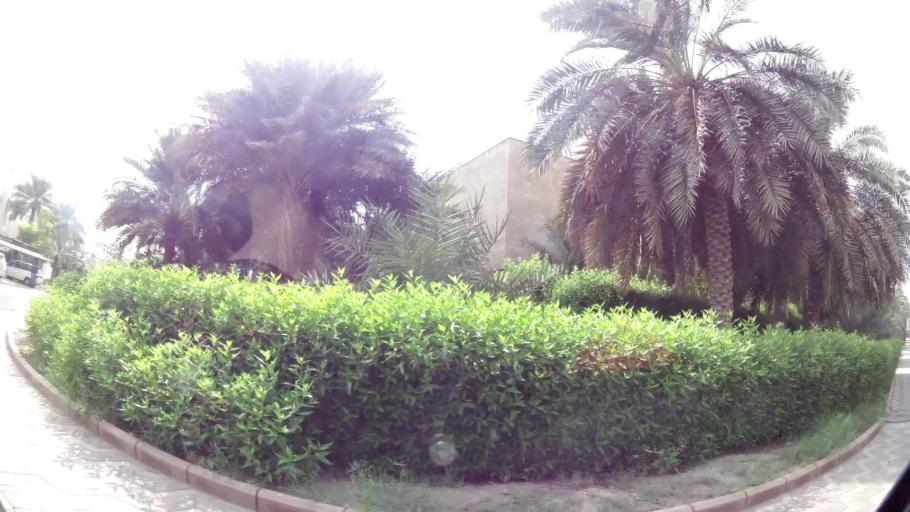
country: KW
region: Al Asimah
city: Ash Shamiyah
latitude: 29.3534
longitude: 47.9755
